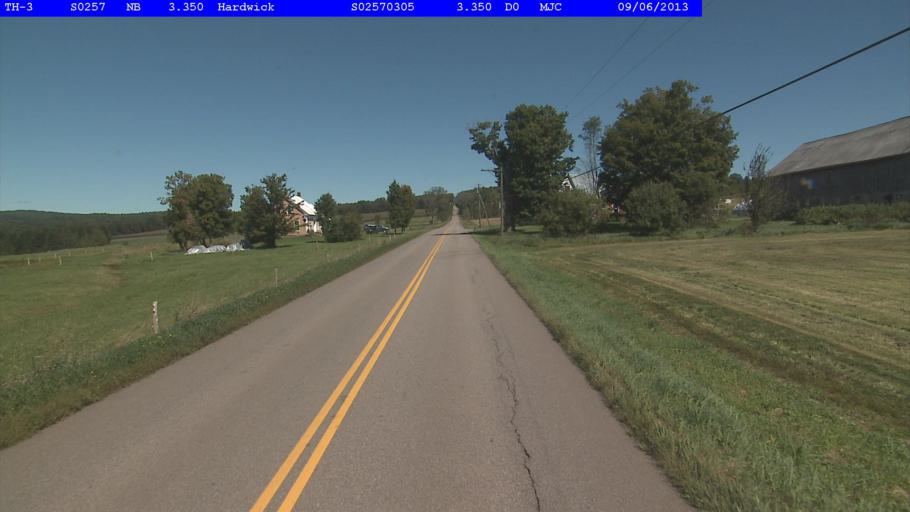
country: US
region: Vermont
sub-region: Caledonia County
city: Hardwick
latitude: 44.5375
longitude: -72.3301
